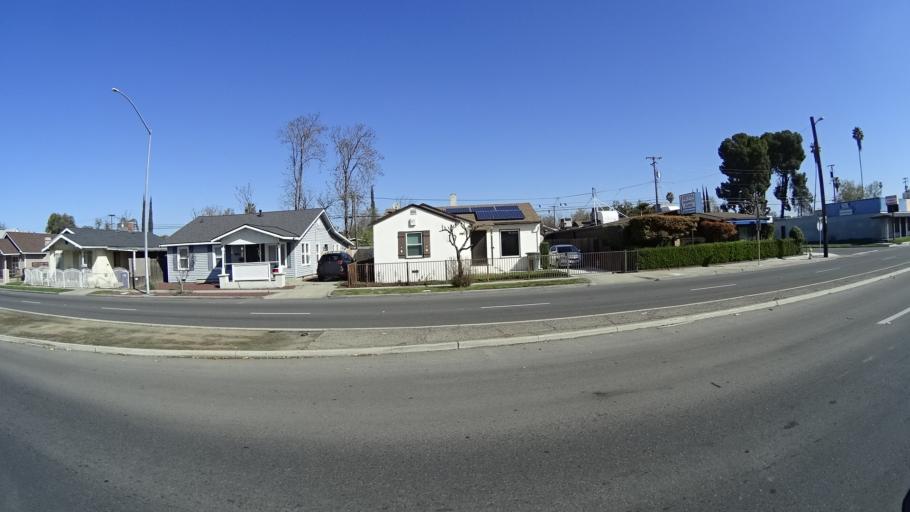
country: US
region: California
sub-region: Fresno County
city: Fresno
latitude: 36.7794
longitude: -119.7932
